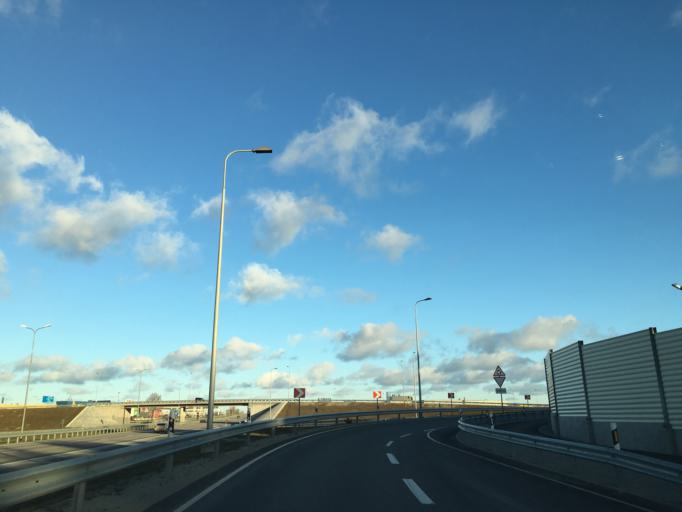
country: EE
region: Harju
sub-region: Saue vald
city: Laagri
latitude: 59.3370
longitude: 24.6100
